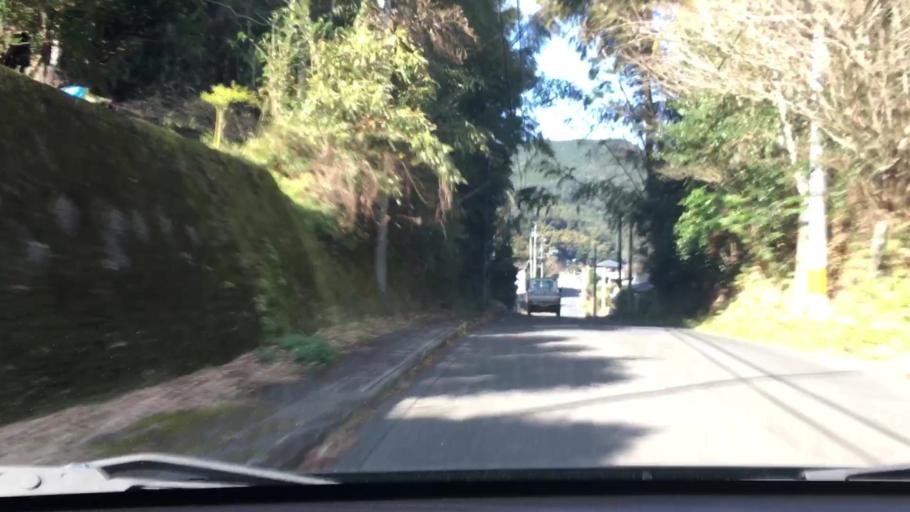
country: JP
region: Kagoshima
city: Ijuin
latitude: 31.7370
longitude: 130.4117
